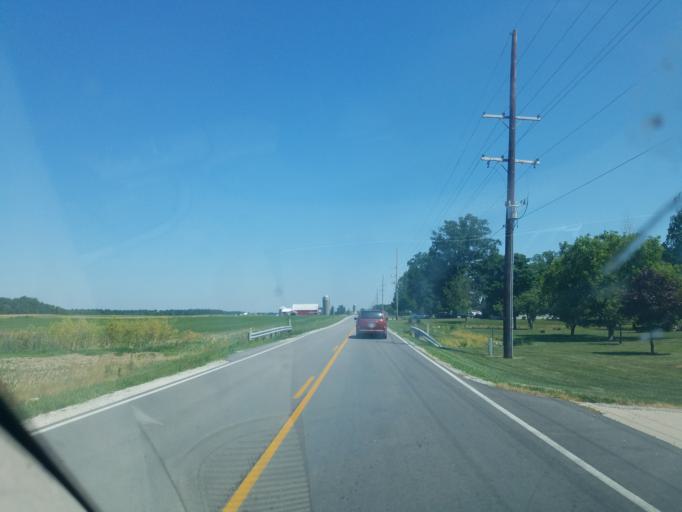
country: US
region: Ohio
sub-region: Mercer County
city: Saint Henry
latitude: 40.4260
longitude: -84.6483
